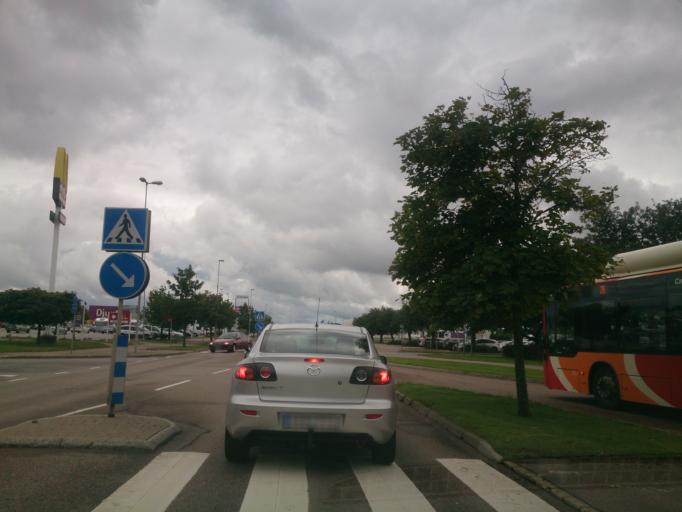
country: SE
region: OEstergoetland
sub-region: Linkopings Kommun
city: Linkoping
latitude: 58.4327
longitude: 15.5886
